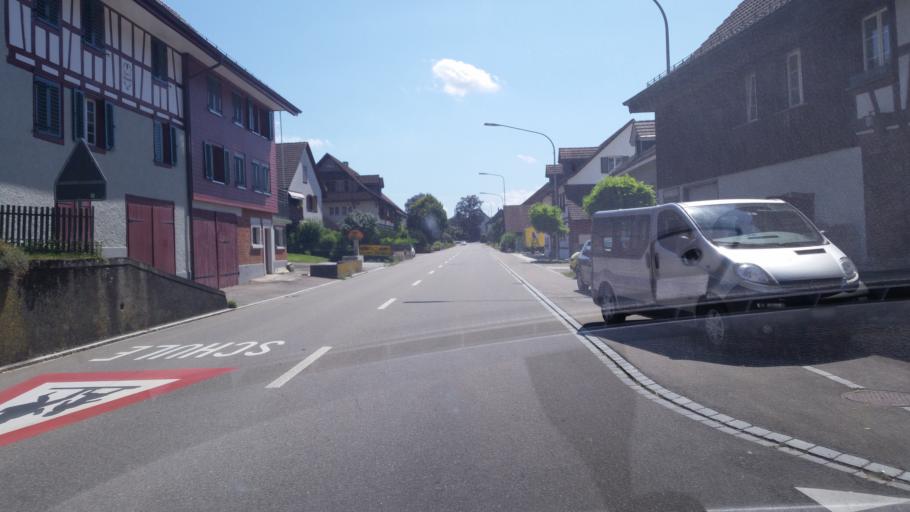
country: CH
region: Zurich
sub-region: Bezirk Buelach
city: Glattfelden
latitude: 47.5587
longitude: 8.5028
